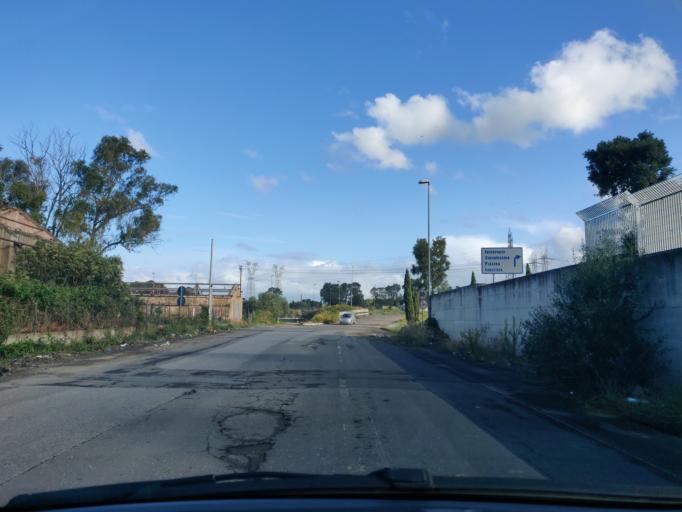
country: IT
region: Latium
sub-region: Citta metropolitana di Roma Capitale
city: Aurelia
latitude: 42.1287
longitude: 11.7876
